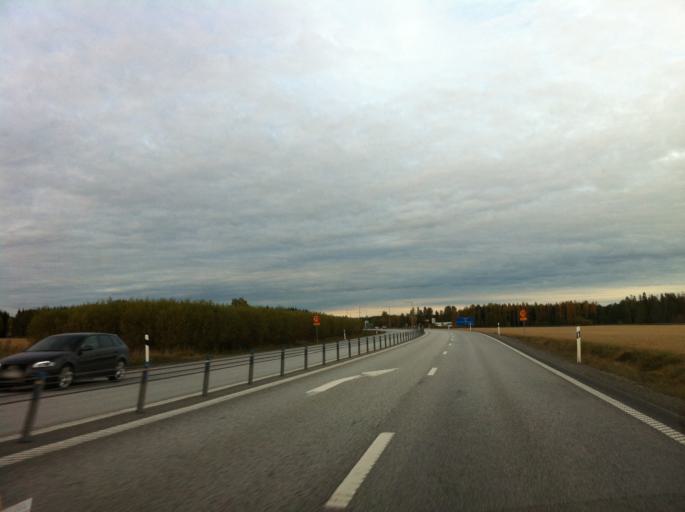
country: SE
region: OErebro
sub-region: Orebro Kommun
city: Hovsta
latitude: 59.4047
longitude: 15.1848
